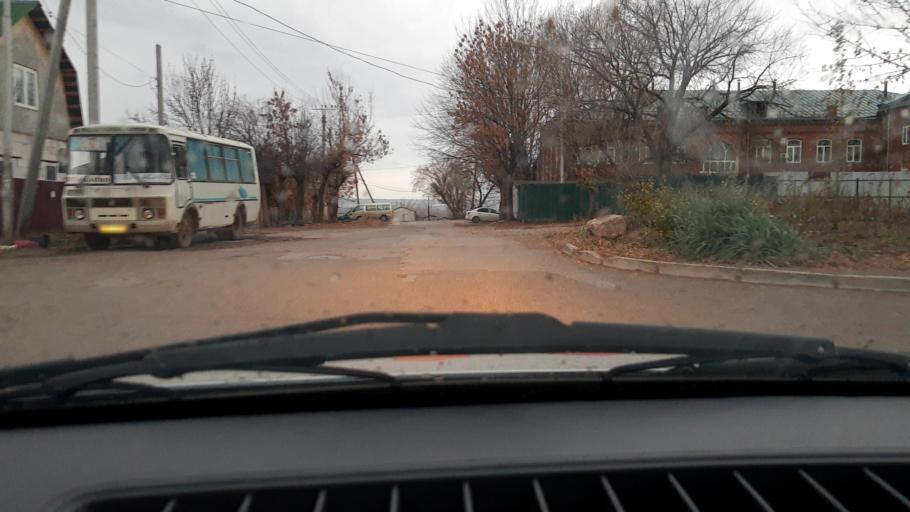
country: RU
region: Bashkortostan
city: Ufa
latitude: 54.7325
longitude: 55.9251
